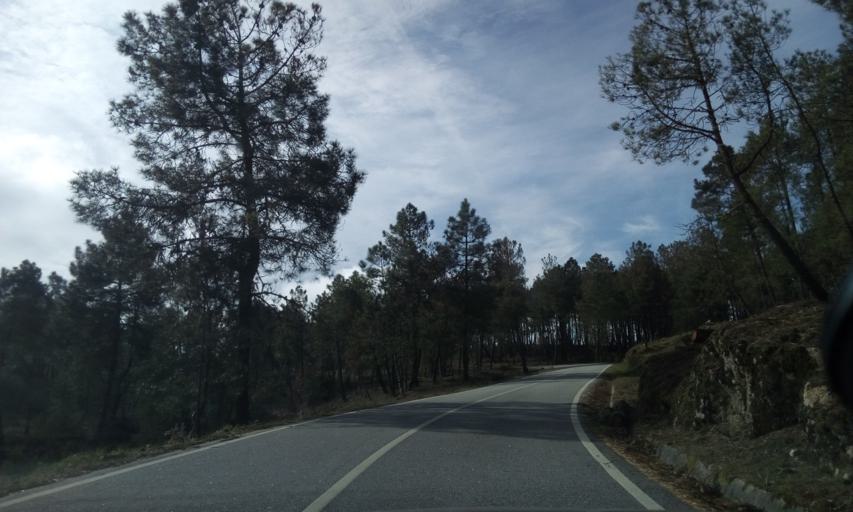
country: PT
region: Guarda
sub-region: Fornos de Algodres
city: Fornos de Algodres
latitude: 40.7062
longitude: -7.5646
